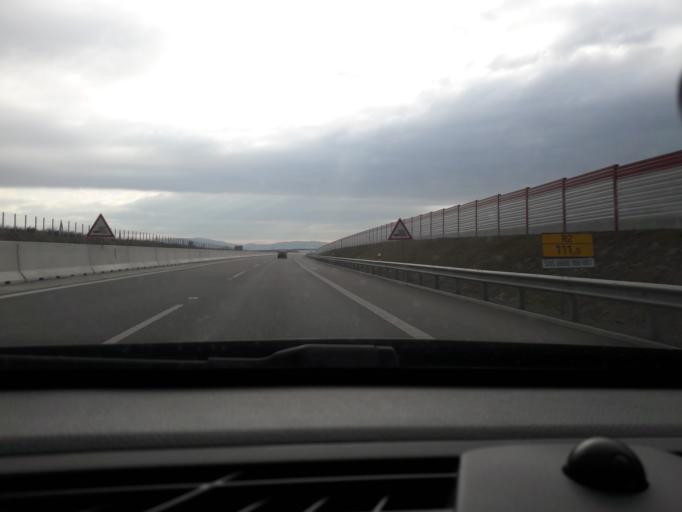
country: SK
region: Banskobystricky
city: Hrochot,Slovakia
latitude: 48.5722
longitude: 19.2639
